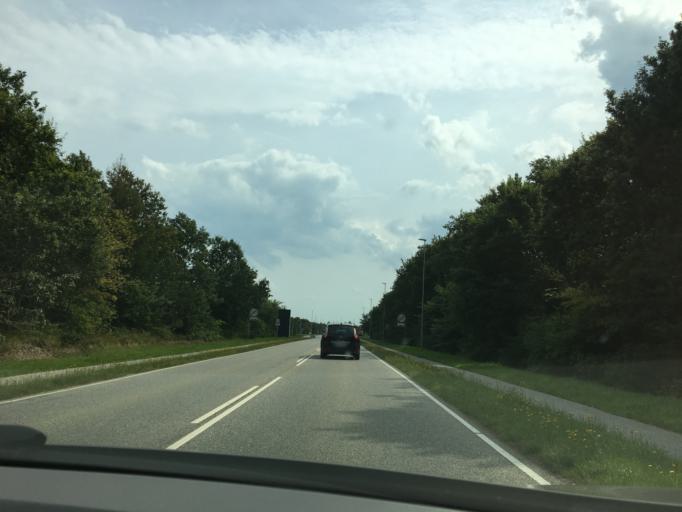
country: DK
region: Central Jutland
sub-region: Skive Kommune
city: Skive
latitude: 56.5472
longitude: 9.0282
